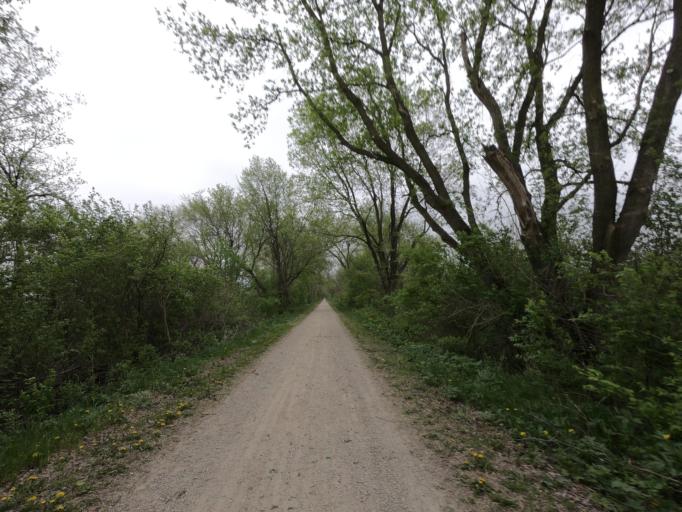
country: US
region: Wisconsin
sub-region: Jefferson County
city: Jefferson
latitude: 43.0449
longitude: -88.8551
